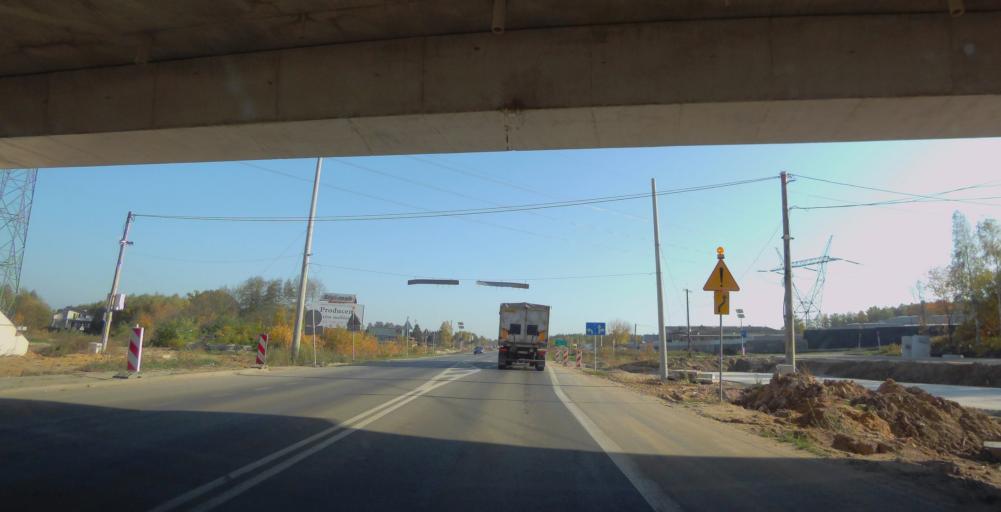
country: PL
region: Masovian Voivodeship
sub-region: Powiat otwocki
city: Celestynow
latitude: 52.1201
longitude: 21.3644
